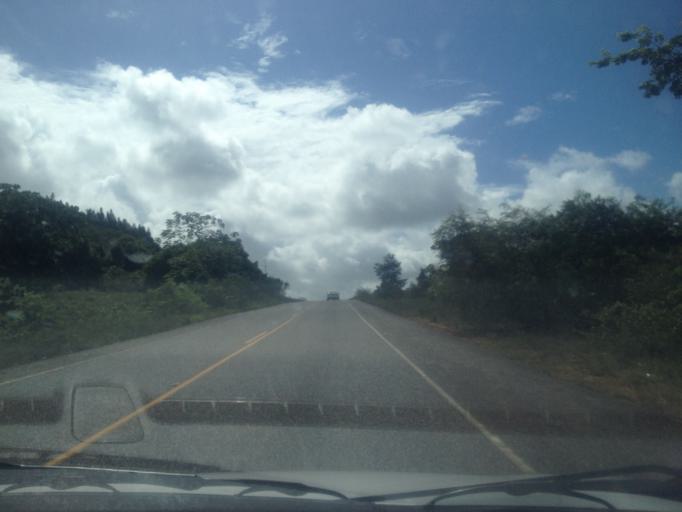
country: BR
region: Bahia
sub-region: Entre Rios
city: Entre Rios
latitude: -12.2244
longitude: -37.8365
